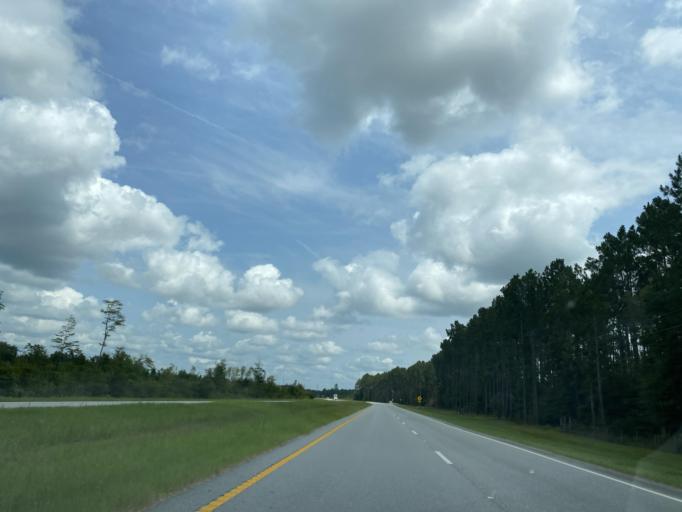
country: US
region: Georgia
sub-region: Ware County
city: Deenwood
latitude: 31.2750
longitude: -82.4477
